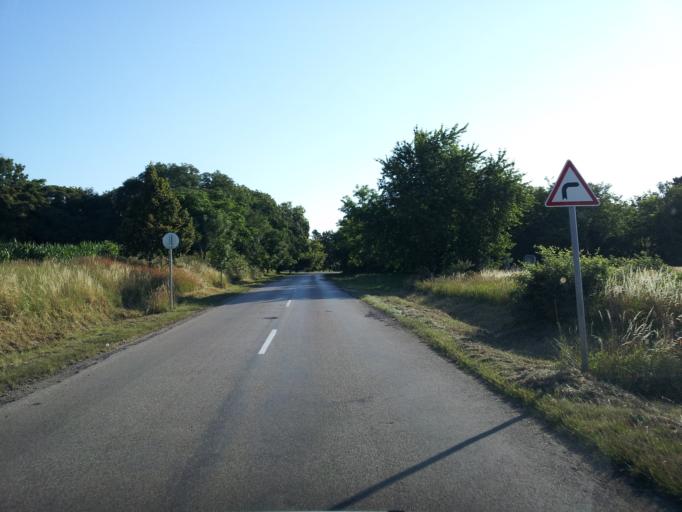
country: HU
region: Fejer
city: Lepseny
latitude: 47.0491
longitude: 18.2407
